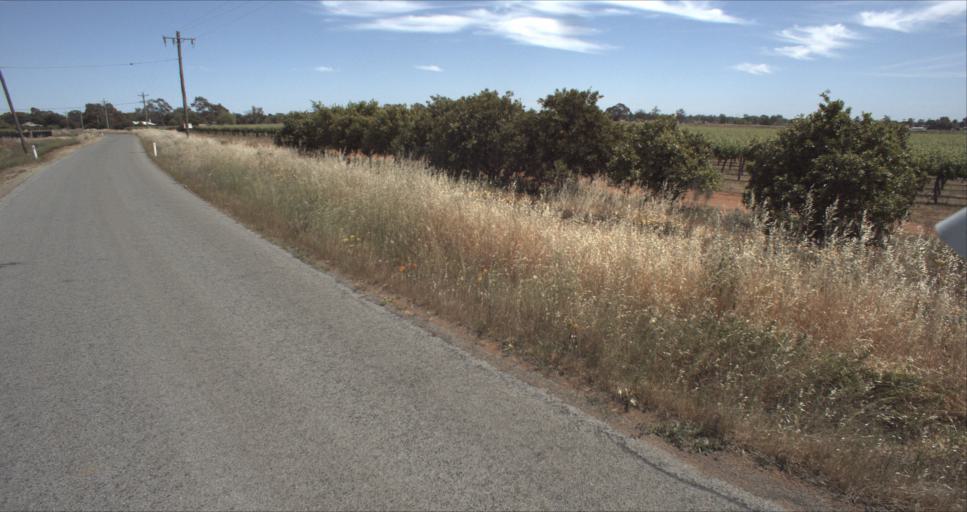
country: AU
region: New South Wales
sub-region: Leeton
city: Leeton
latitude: -34.5700
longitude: 146.4408
